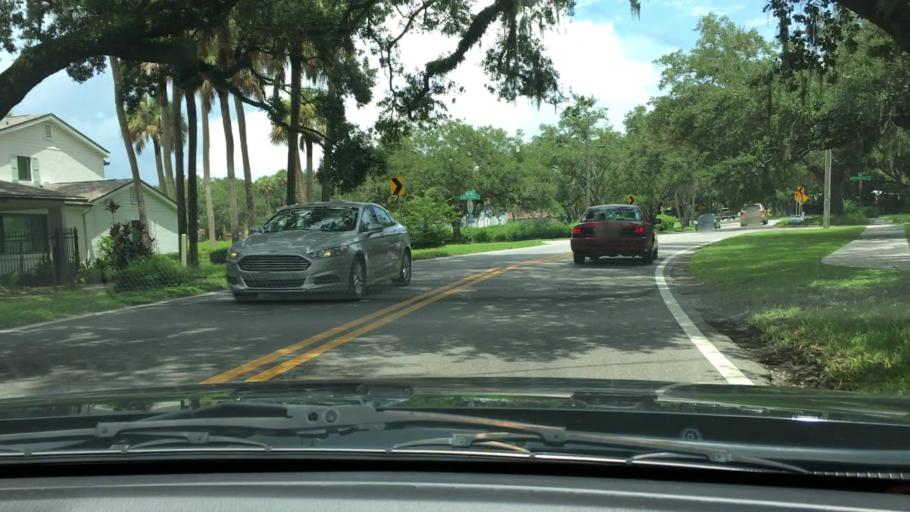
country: US
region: Florida
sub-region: Hillsborough County
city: Tampa
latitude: 27.9207
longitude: -82.5235
